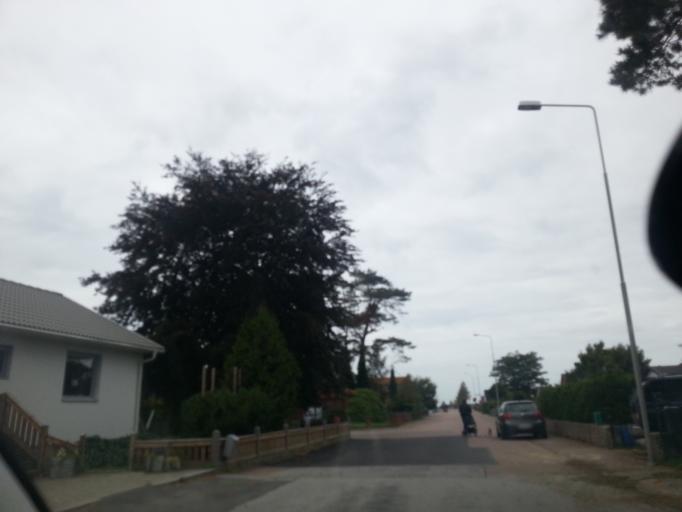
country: SE
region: Skane
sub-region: Landskrona
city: Asmundtorp
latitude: 55.8534
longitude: 12.9134
